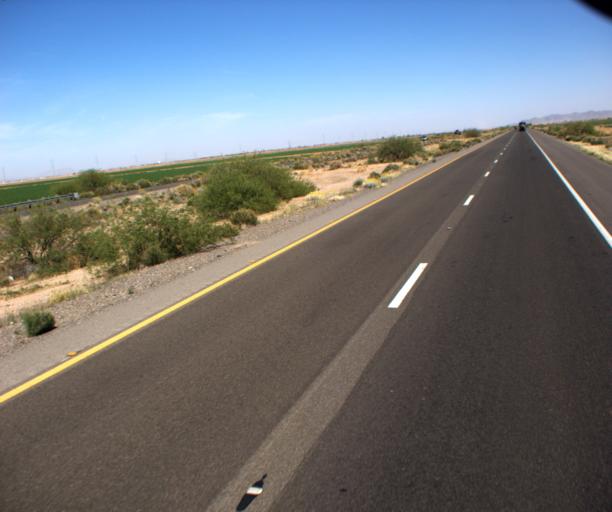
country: US
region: Arizona
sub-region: Pinal County
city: Casa Grande
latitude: 32.8280
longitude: -111.9111
